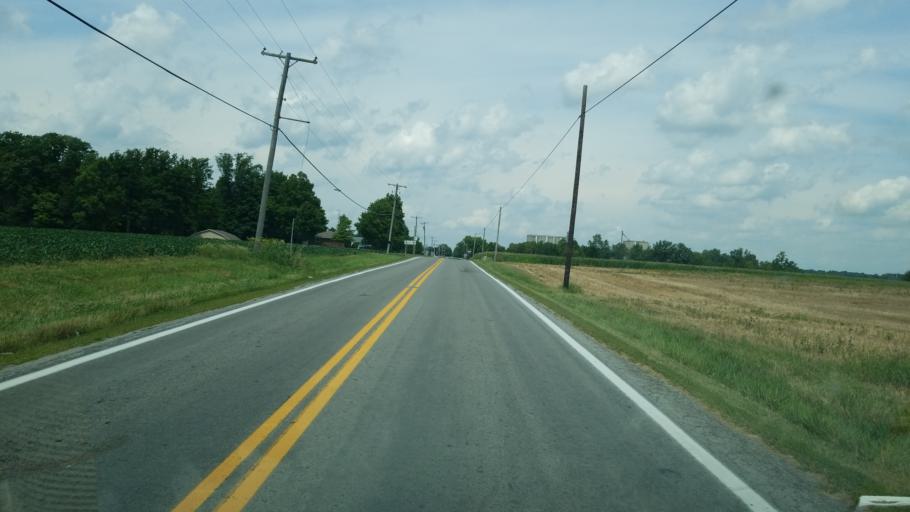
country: US
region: Ohio
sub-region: Hancock County
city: Arlington
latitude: 40.8921
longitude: -83.7276
